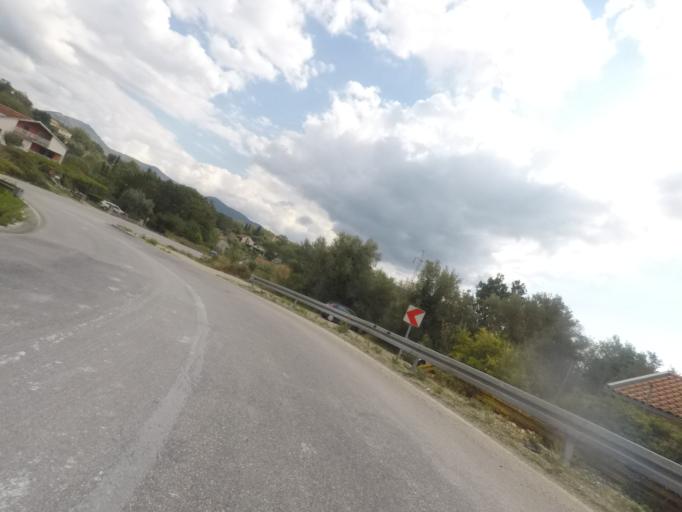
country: ME
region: Herceg Novi
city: Herceg-Novi
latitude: 42.4635
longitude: 18.5459
